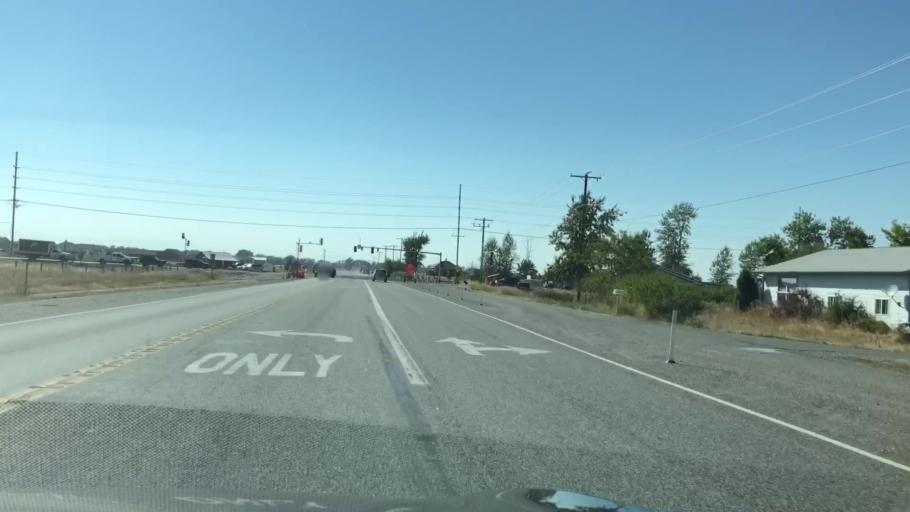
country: US
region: Montana
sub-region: Gallatin County
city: Belgrade
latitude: 45.7292
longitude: -111.1830
